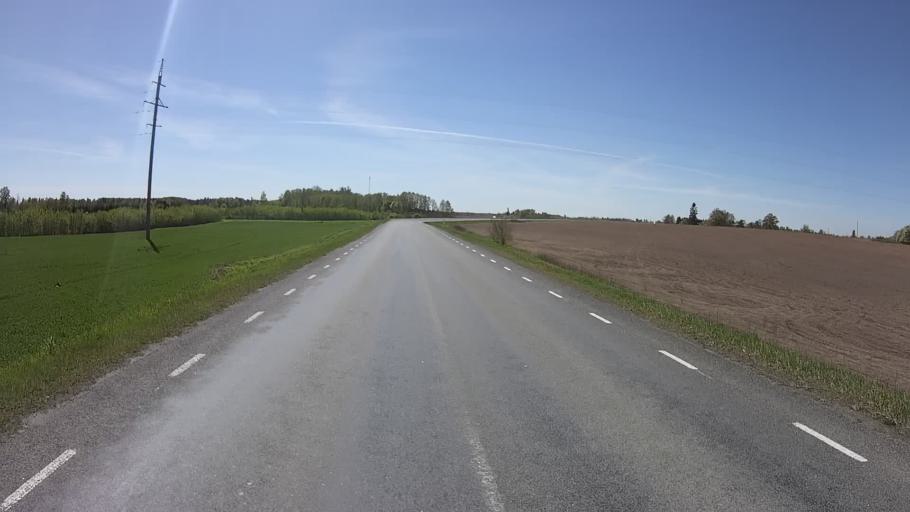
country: EE
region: Harju
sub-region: Raasiku vald
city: Raasiku
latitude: 59.1197
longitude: 25.1875
